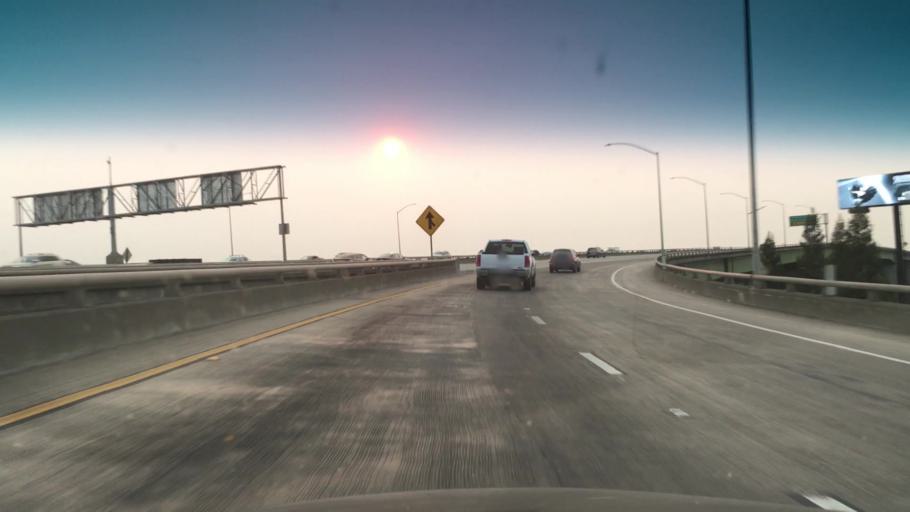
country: US
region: California
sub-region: Yolo County
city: West Sacramento
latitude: 38.5696
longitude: -121.5130
